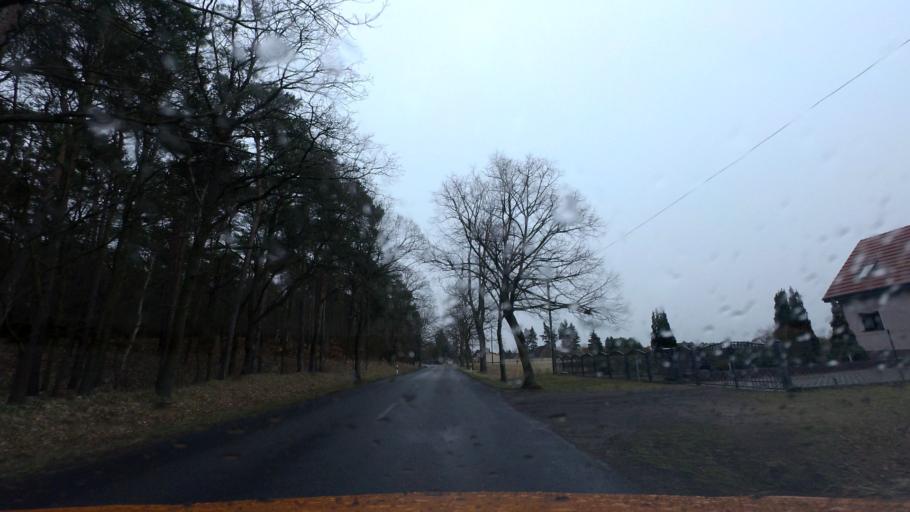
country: DE
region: Brandenburg
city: Brieselang
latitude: 52.6411
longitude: 13.0331
